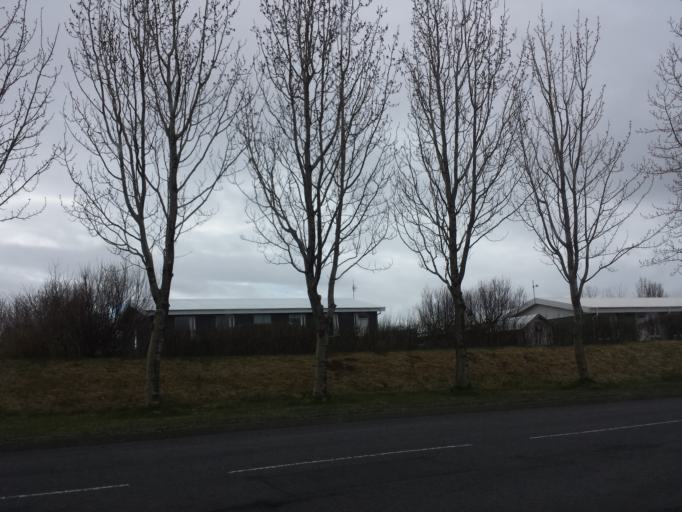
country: IS
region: Capital Region
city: Gardabaer
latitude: 64.0905
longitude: -21.8949
